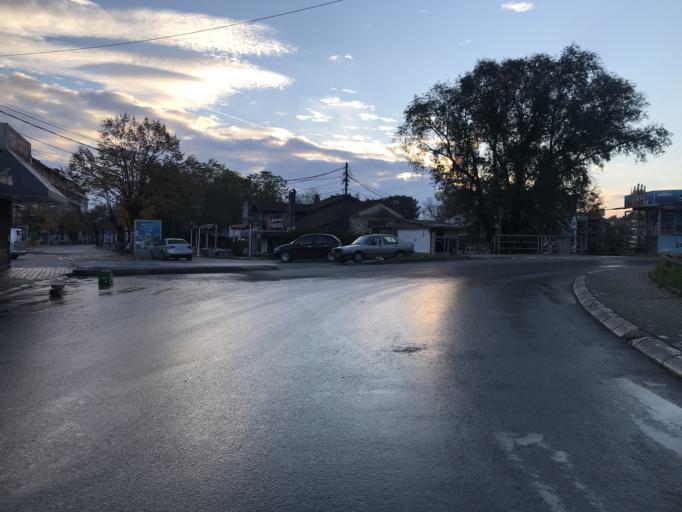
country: XK
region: Pec
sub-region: Komuna e Pejes
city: Peje
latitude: 42.6590
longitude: 20.2858
